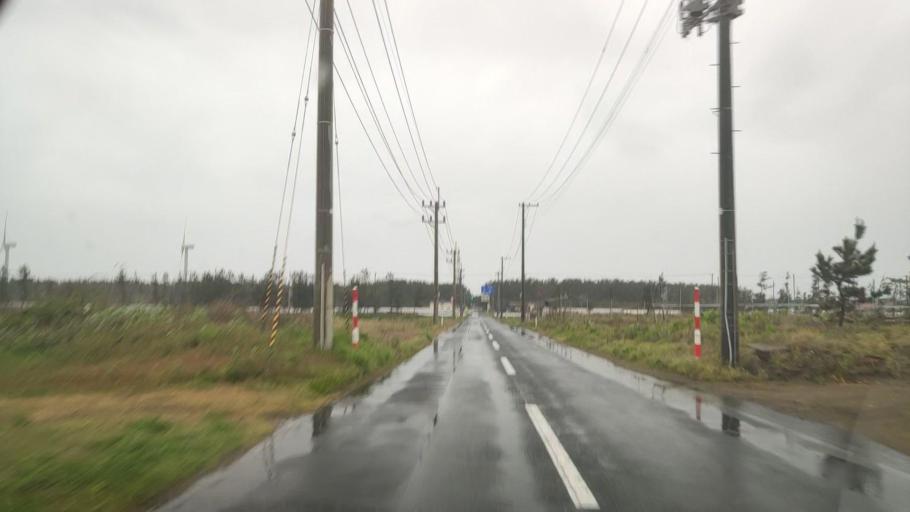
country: JP
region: Akita
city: Noshiromachi
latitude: 40.0971
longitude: 139.9690
